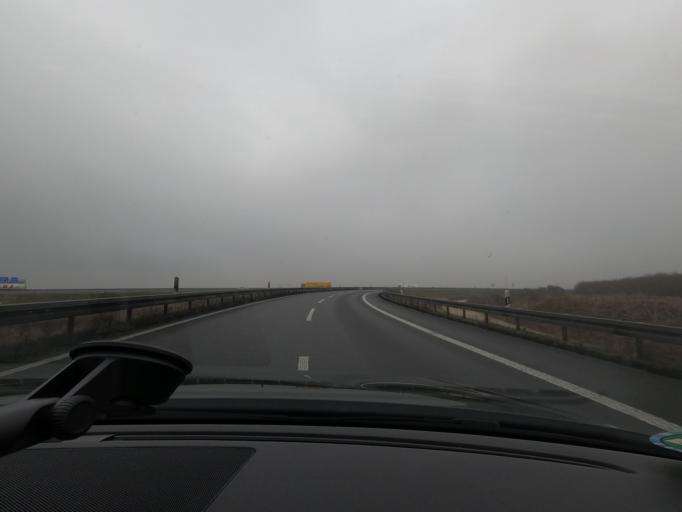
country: DE
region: North Rhine-Westphalia
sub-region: Regierungsbezirk Koln
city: Titz
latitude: 51.0325
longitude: 6.4775
